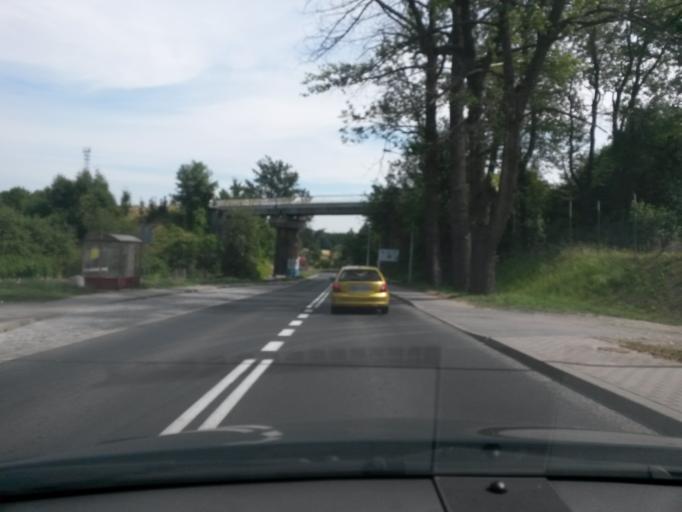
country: PL
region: Lower Silesian Voivodeship
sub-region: Powiat jeleniogorski
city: Janowice Wielkie
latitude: 50.9095
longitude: 15.9589
